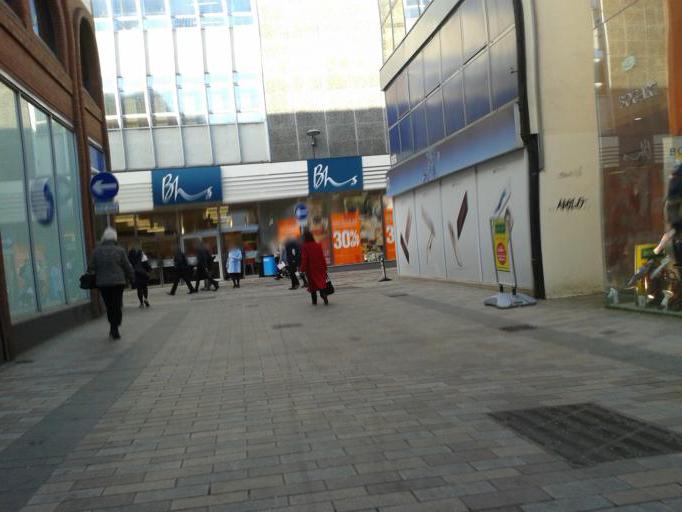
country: GB
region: Northern Ireland
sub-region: City of Belfast
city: Belfast
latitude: 54.5981
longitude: -5.9285
